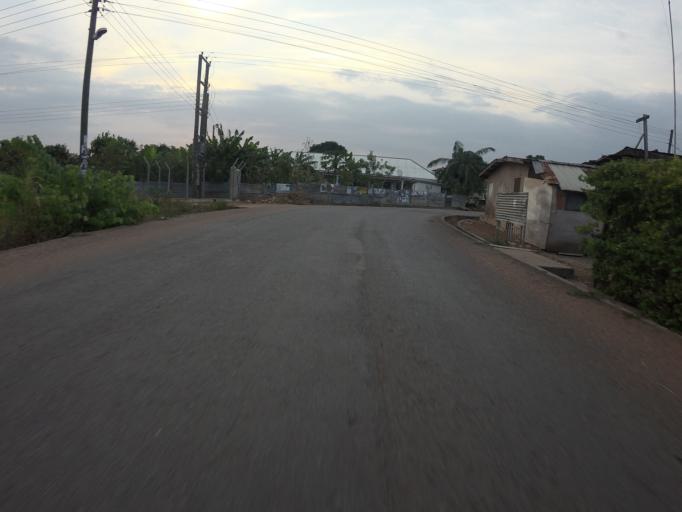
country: GH
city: Akropong
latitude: 6.1000
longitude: -0.0134
